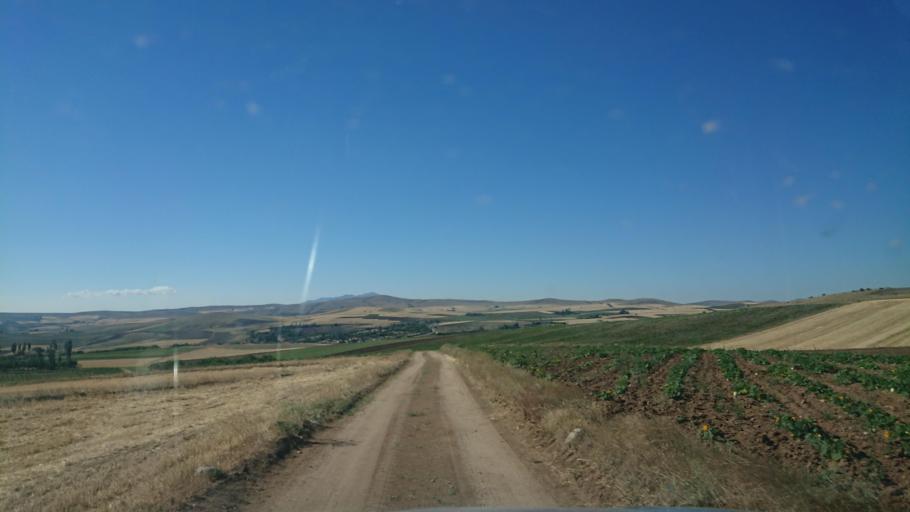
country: TR
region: Aksaray
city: Agacoren
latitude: 38.8344
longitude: 33.9480
